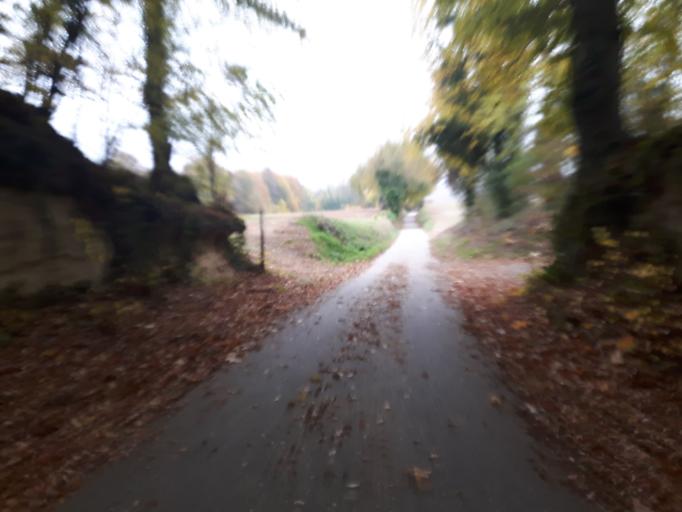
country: DE
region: Baden-Wuerttemberg
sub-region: Karlsruhe Region
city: Ostringen
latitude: 49.1935
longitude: 8.7308
